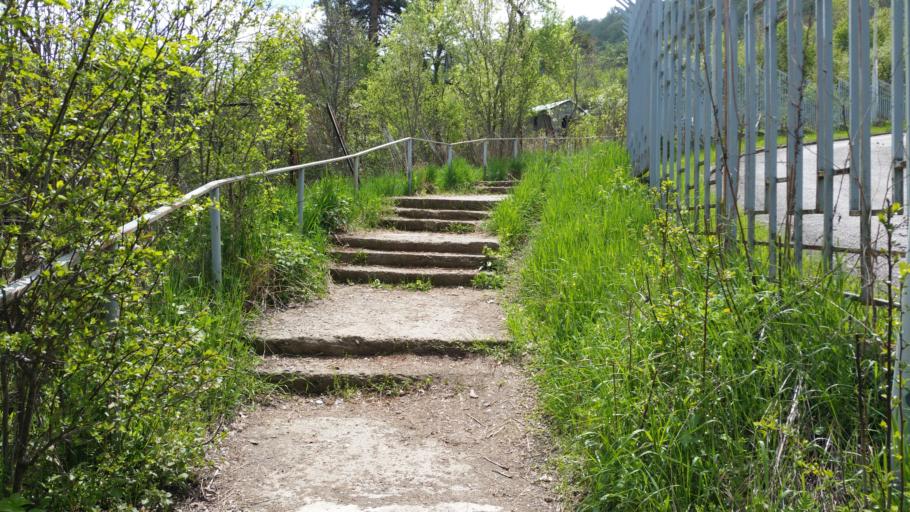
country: AM
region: Tavush
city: Dilijan
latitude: 40.7385
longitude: 44.8429
